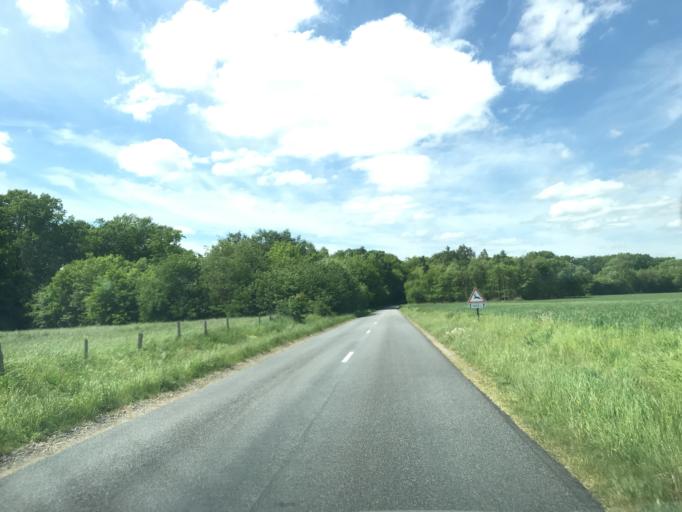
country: FR
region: Haute-Normandie
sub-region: Departement de l'Eure
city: Beaumont-le-Roger
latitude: 49.1501
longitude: 0.8217
